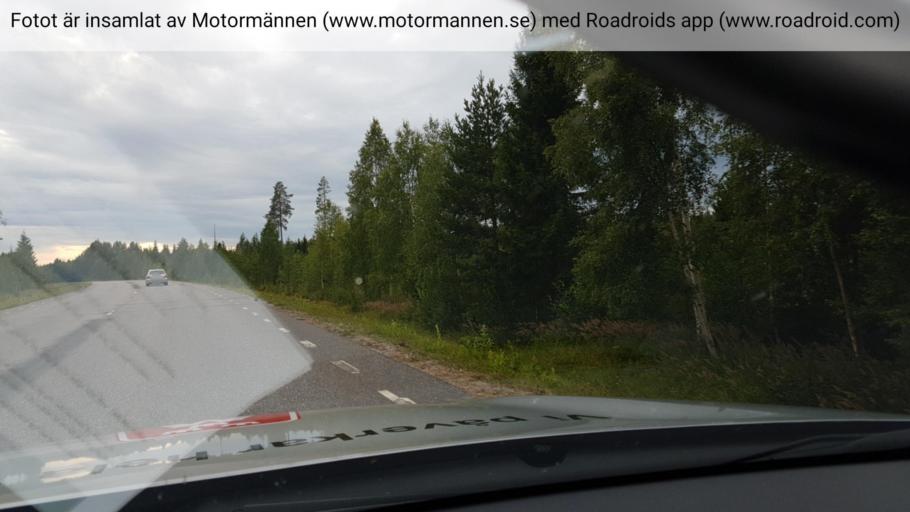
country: SE
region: Norrbotten
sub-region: Lulea Kommun
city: Gammelstad
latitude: 65.6633
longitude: 22.0715
